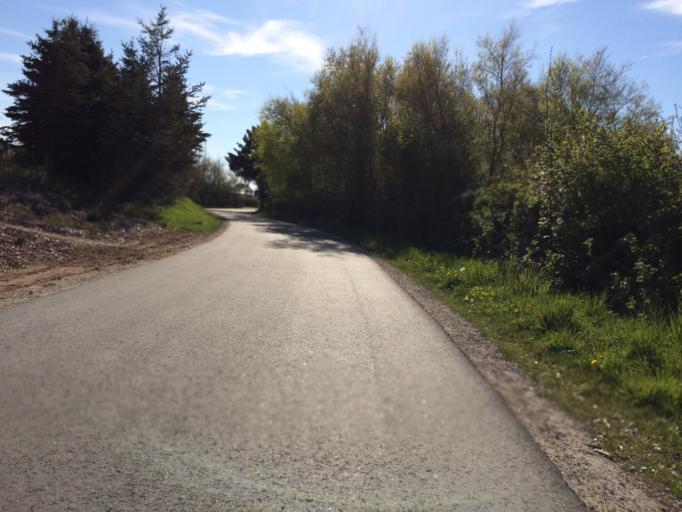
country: DK
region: Central Jutland
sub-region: Struer Kommune
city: Struer
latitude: 56.5501
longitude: 8.6216
